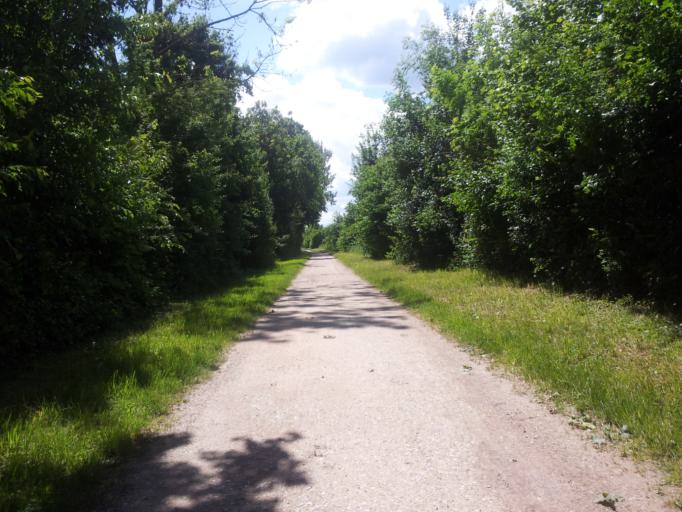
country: DE
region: Baden-Wuerttemberg
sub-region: Regierungsbezirk Stuttgart
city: Kongen
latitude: 48.6807
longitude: 9.3735
